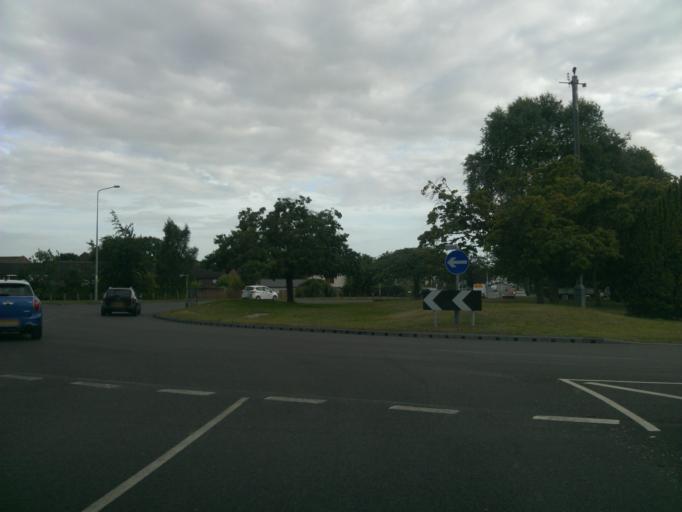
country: GB
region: England
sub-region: Essex
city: Clacton-on-Sea
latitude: 51.8051
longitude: 1.1485
